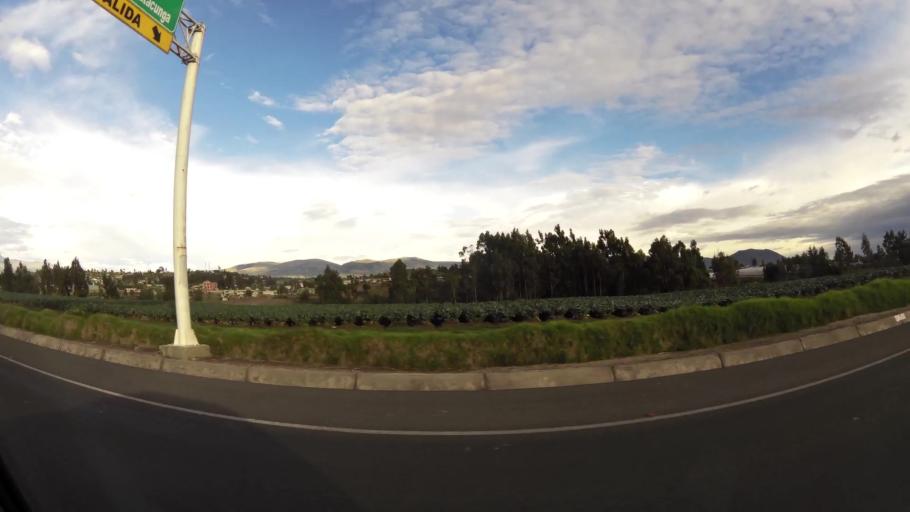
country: EC
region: Cotopaxi
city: Saquisili
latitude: -0.8558
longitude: -78.6210
